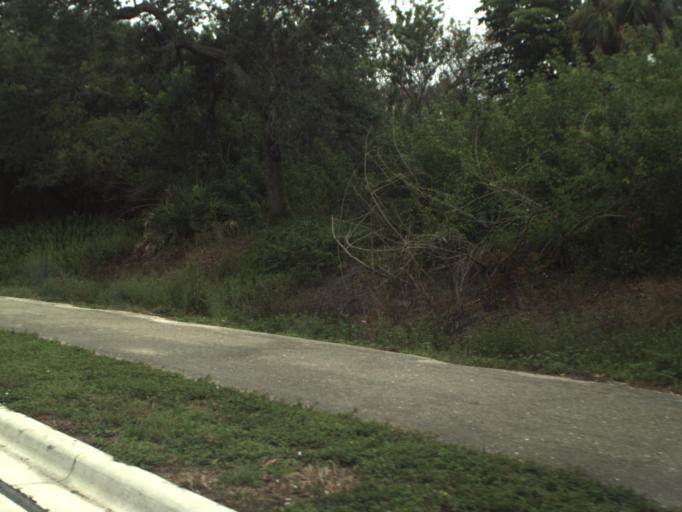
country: US
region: Florida
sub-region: Palm Beach County
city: Boca Del Mar
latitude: 26.3506
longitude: -80.1227
